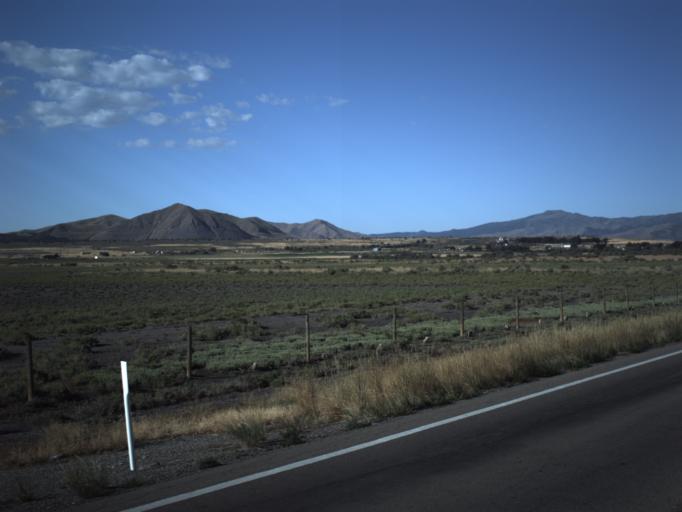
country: US
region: Utah
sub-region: Utah County
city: Genola
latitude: 39.9566
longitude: -111.8808
